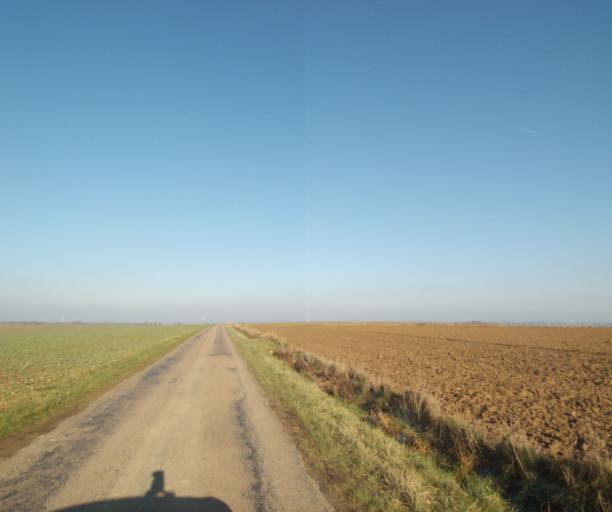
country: FR
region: Champagne-Ardenne
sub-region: Departement de la Haute-Marne
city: Chevillon
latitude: 48.5044
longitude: 5.0826
